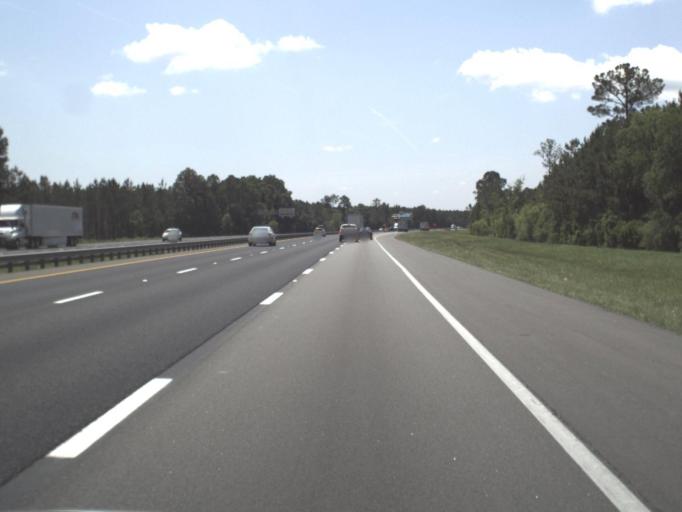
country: US
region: Florida
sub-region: Nassau County
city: Yulee
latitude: 30.6080
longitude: -81.6461
